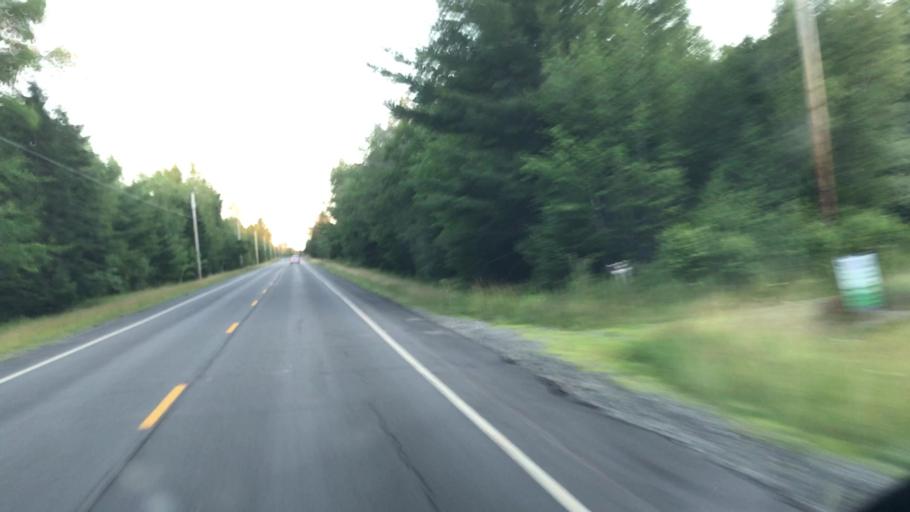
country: US
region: Maine
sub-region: Penobscot County
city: Medway
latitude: 45.5740
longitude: -68.3204
